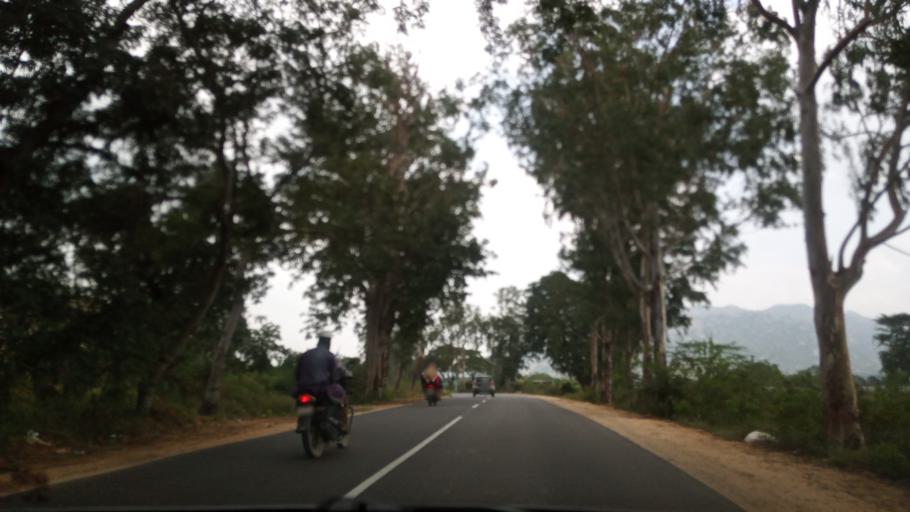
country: IN
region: Andhra Pradesh
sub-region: Chittoor
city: Madanapalle
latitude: 13.6371
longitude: 78.5782
